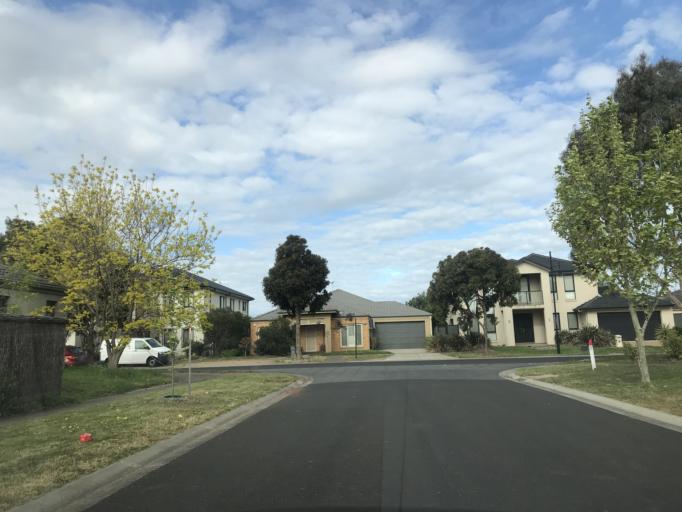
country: AU
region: Victoria
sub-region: Wyndham
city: Williams Landing
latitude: -37.8861
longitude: 144.7379
